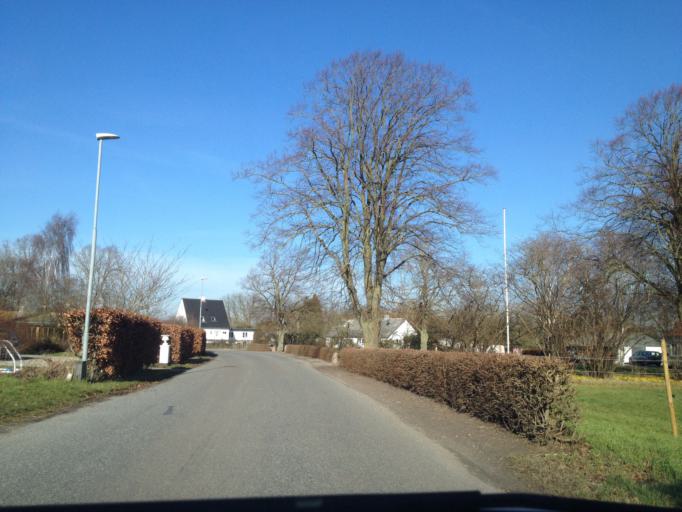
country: DK
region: South Denmark
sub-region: Nyborg Kommune
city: Ullerslev
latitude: 55.3876
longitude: 10.7065
